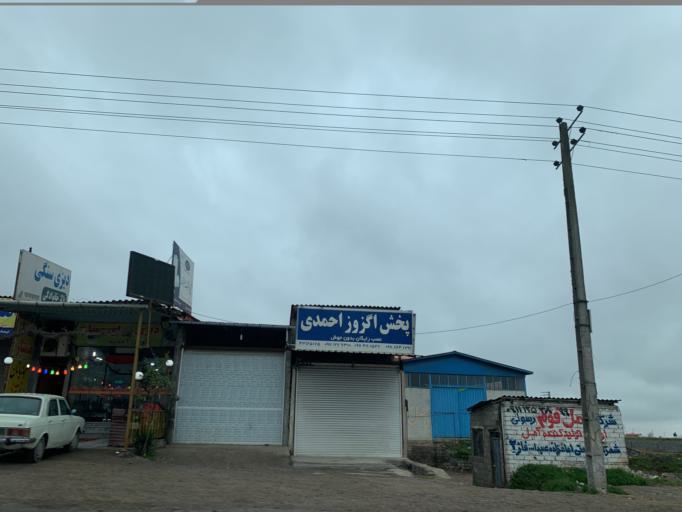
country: IR
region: Mazandaran
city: Amol
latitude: 36.4162
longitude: 52.3487
